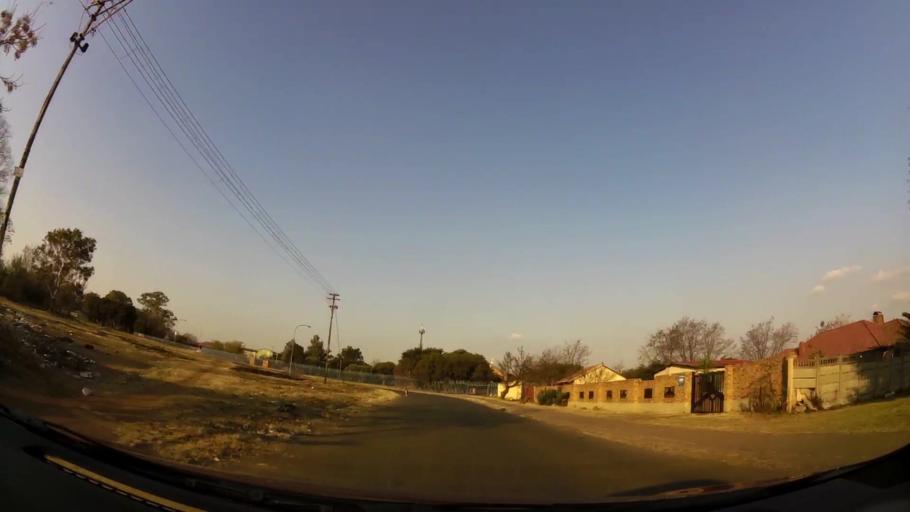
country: ZA
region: Gauteng
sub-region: City of Johannesburg Metropolitan Municipality
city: Soweto
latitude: -26.2847
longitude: 27.8979
